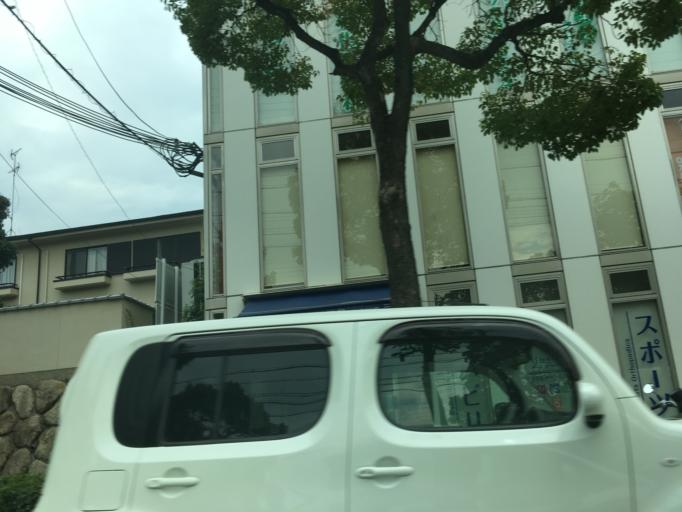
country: JP
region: Hyogo
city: Ashiya
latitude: 34.7232
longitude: 135.2608
